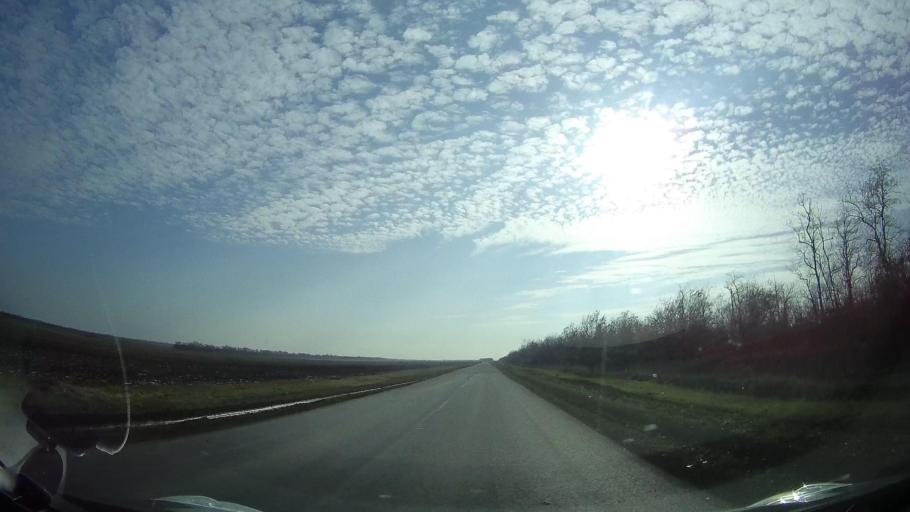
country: RU
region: Rostov
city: Veselyy
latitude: 46.9755
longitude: 40.7198
